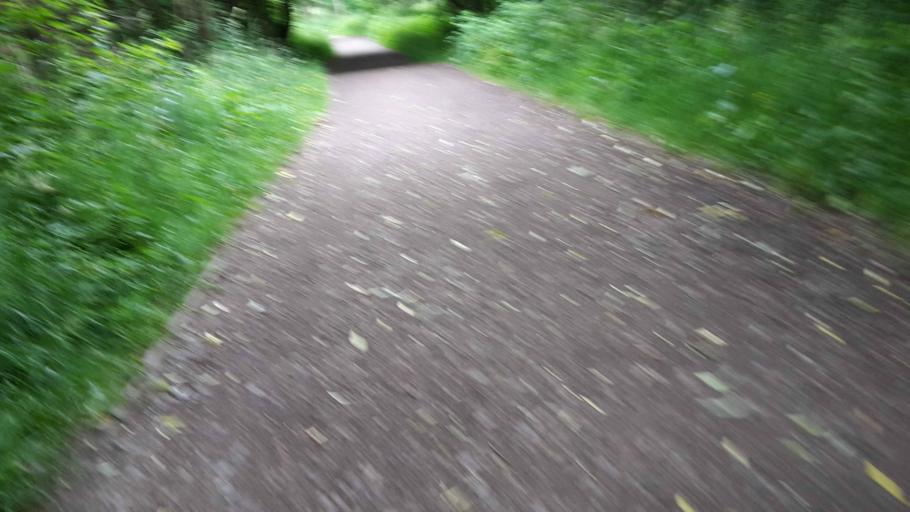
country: GB
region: Scotland
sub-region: South Lanarkshire
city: Uddingston
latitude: 55.8213
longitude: -4.0935
